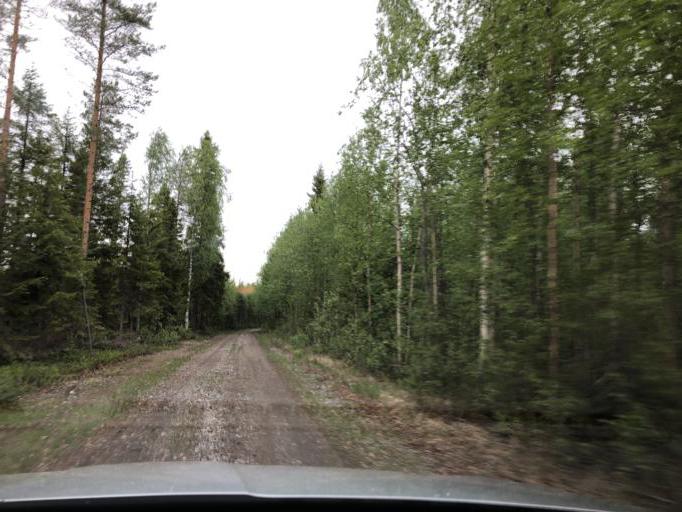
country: SE
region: Norrbotten
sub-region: Pitea Kommun
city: Roknas
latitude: 65.4022
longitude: 21.2619
